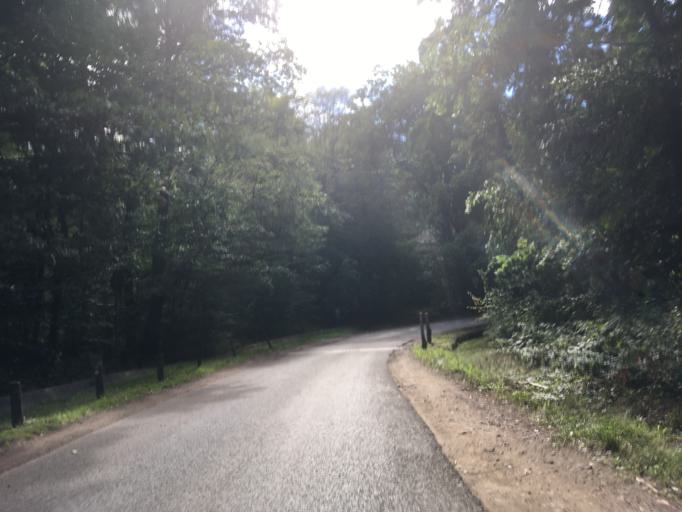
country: DE
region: Brandenburg
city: Oderberg
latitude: 52.9109
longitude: 14.0162
